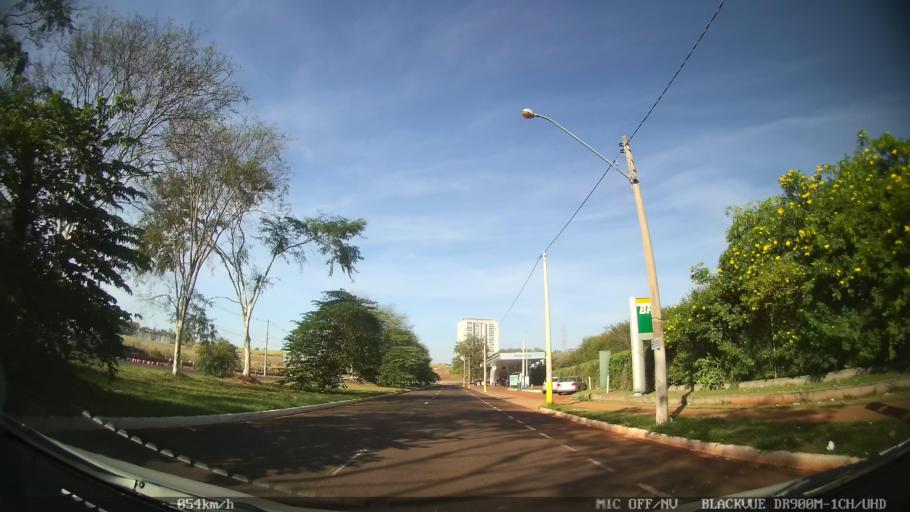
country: BR
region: Sao Paulo
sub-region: Ribeirao Preto
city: Ribeirao Preto
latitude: -21.2223
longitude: -47.8065
